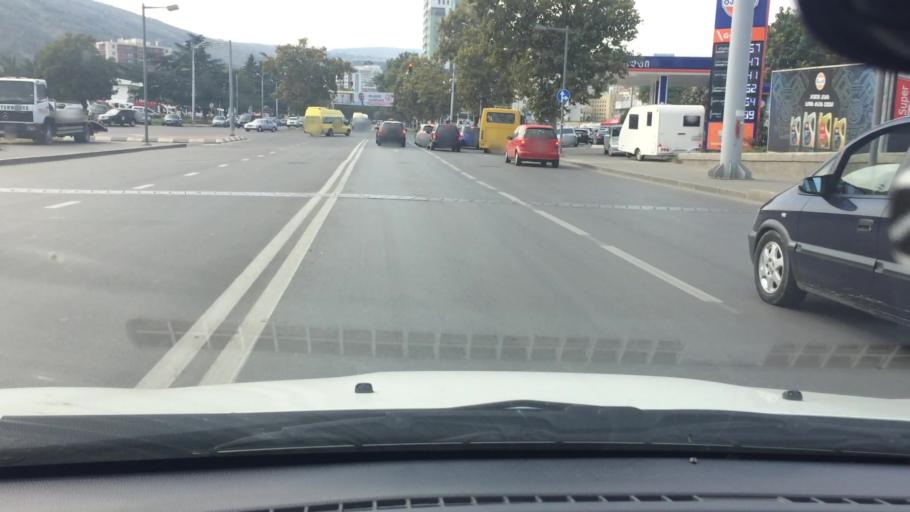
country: GE
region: T'bilisi
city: Tbilisi
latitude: 41.6763
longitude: 44.8365
